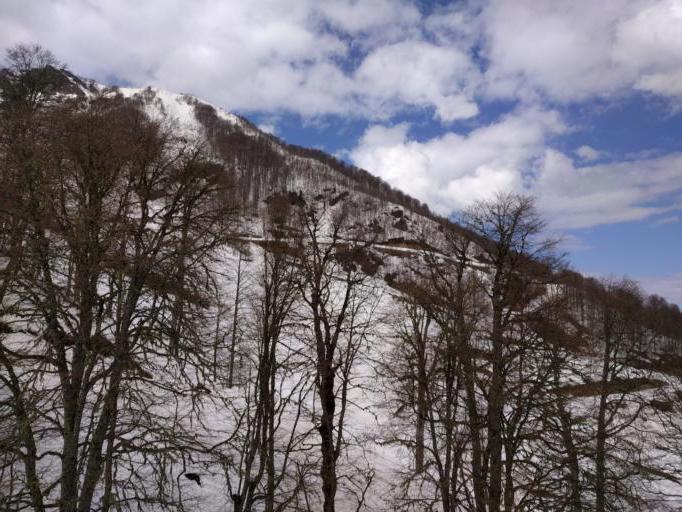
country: RU
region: Krasnodarskiy
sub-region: Sochi City
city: Krasnaya Polyana
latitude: 43.6367
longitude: 40.3130
